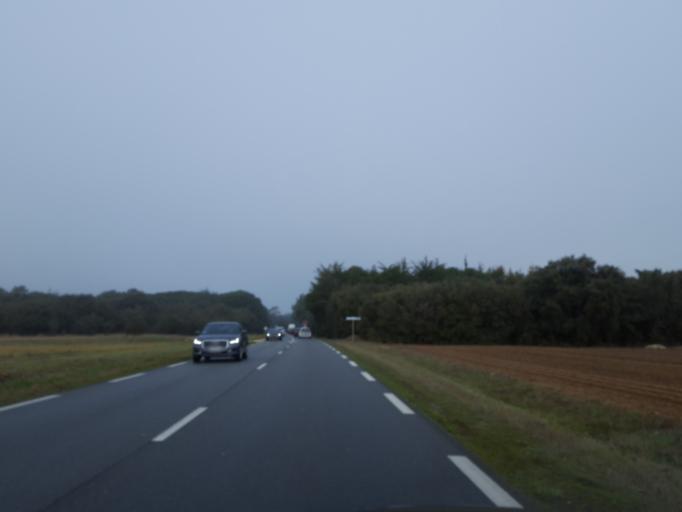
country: FR
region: Poitou-Charentes
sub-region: Departement de la Charente-Maritime
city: La Flotte
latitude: 46.1858
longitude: -1.3406
